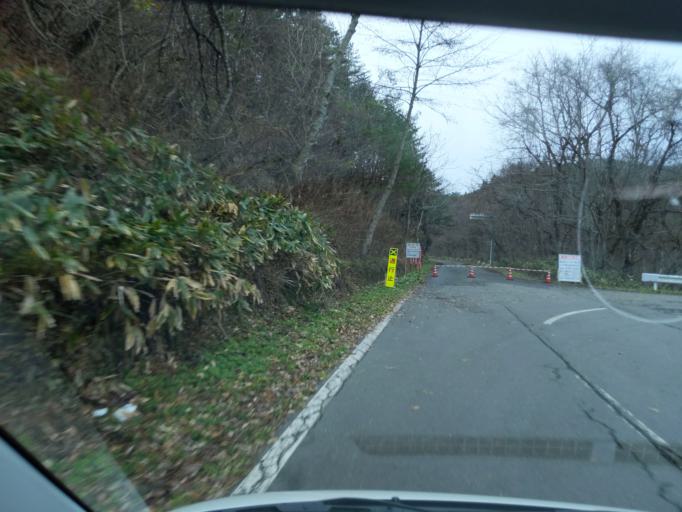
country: JP
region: Iwate
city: Tono
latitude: 39.1572
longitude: 141.3667
